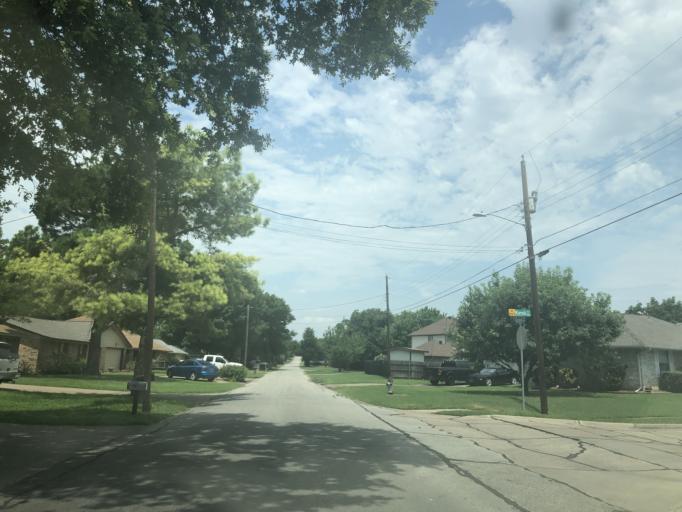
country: US
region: Texas
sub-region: Dallas County
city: Irving
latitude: 32.7887
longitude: -96.9371
